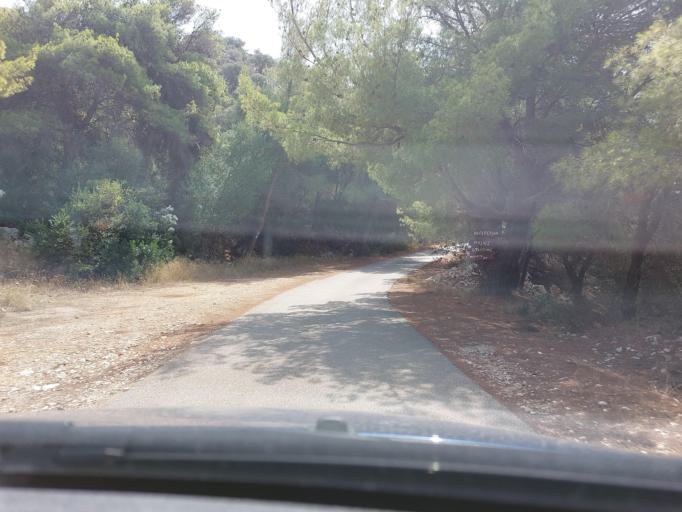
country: HR
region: Dubrovacko-Neretvanska
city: Smokvica
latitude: 42.7314
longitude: 16.8926
